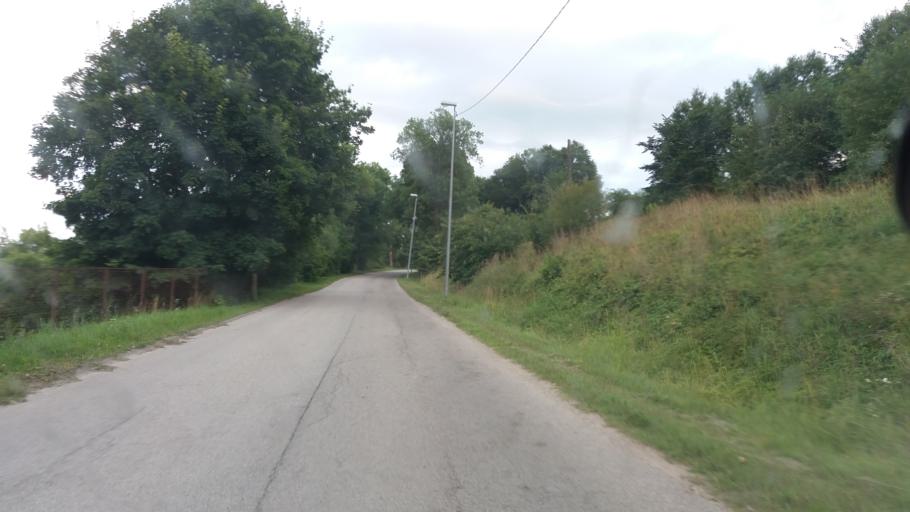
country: LV
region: Talsu Rajons
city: Sabile
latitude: 57.0405
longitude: 22.5685
